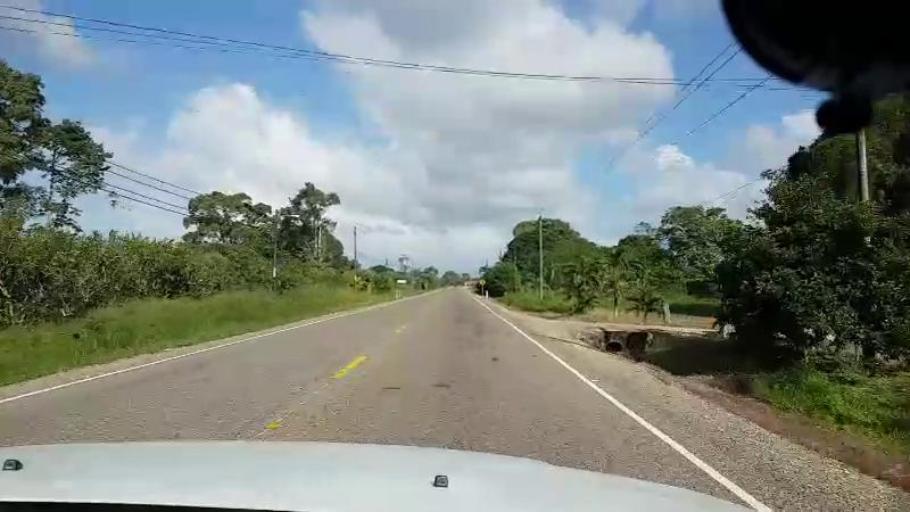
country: BZ
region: Stann Creek
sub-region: Dangriga
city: Dangriga
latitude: 16.9967
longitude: -88.3542
